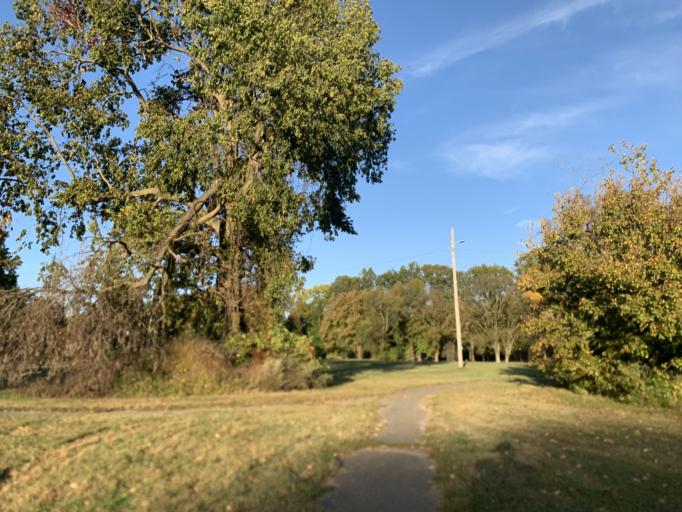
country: US
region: Kentucky
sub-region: Jefferson County
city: Shively
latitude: 38.2412
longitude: -85.8324
